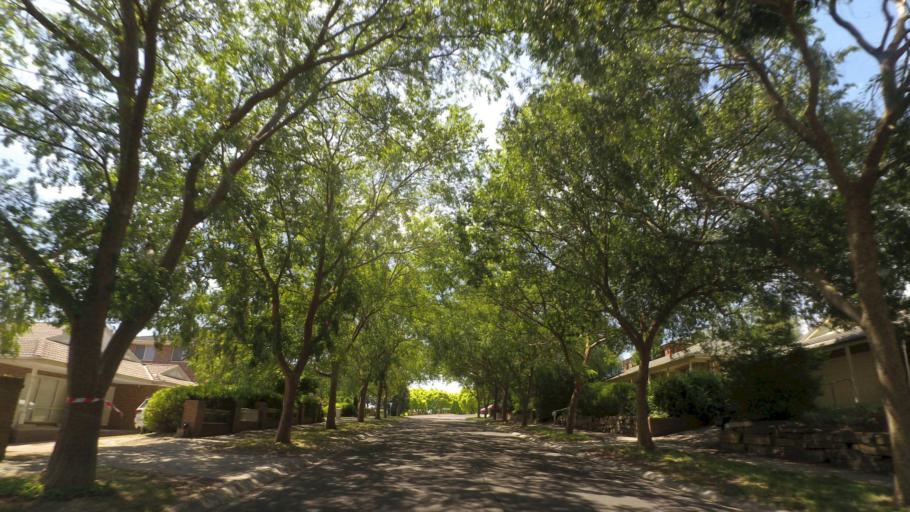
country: AU
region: Victoria
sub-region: Yarra Ranges
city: Chirnside Park
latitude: -37.7579
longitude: 145.3054
